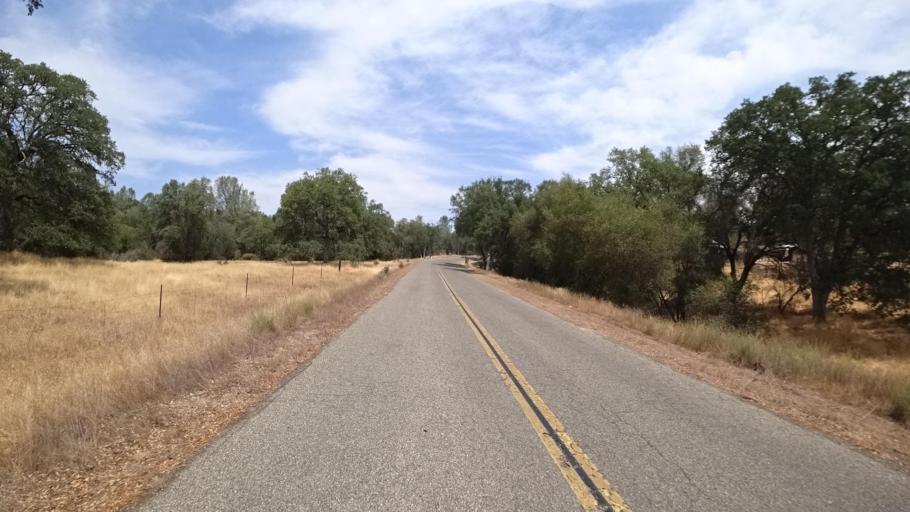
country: US
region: California
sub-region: Mariposa County
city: Mariposa
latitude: 37.4259
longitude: -119.8598
